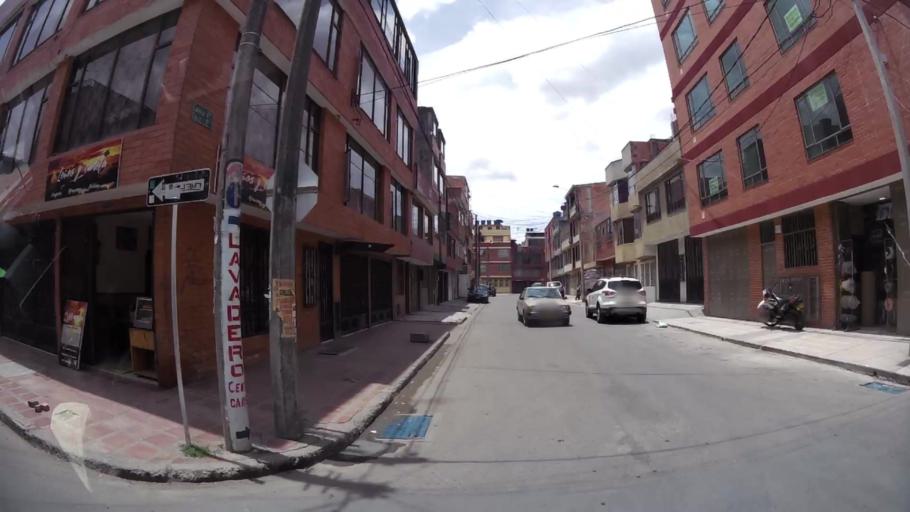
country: CO
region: Bogota D.C.
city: Bogota
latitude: 4.6445
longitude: -74.1468
